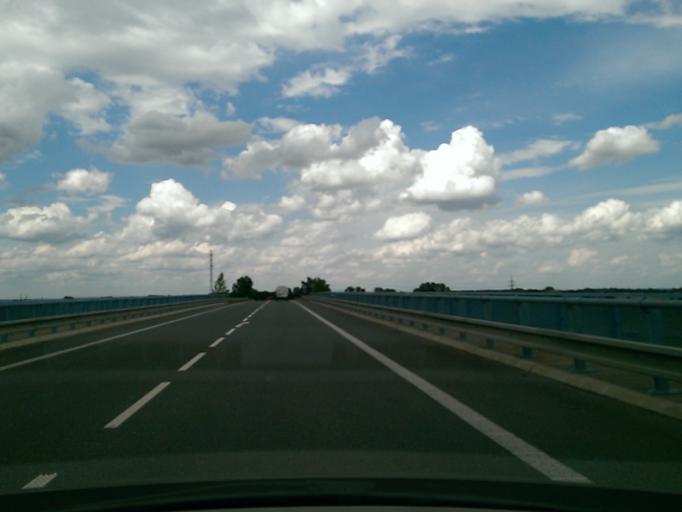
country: CZ
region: Central Bohemia
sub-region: Okres Nymburk
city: Podebrady
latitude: 50.1669
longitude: 15.0905
